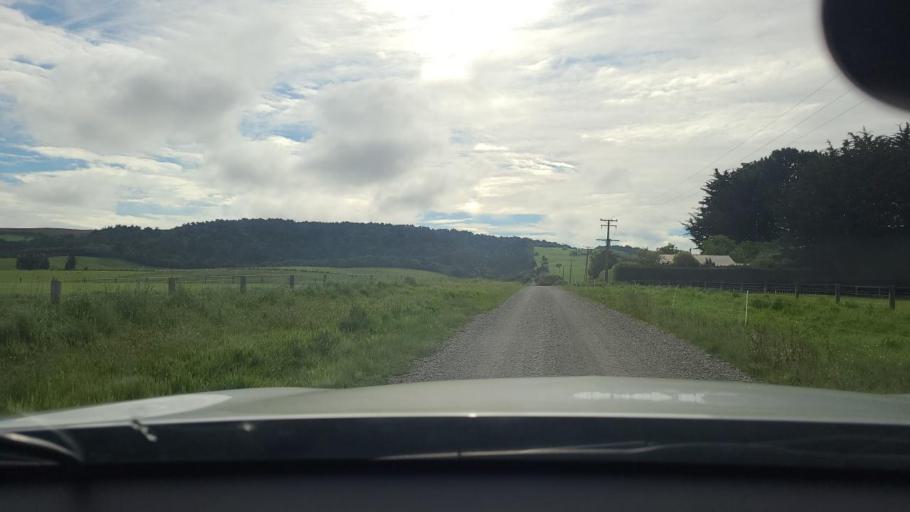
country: NZ
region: Southland
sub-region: Southland District
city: Winton
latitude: -46.2050
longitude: 168.4134
